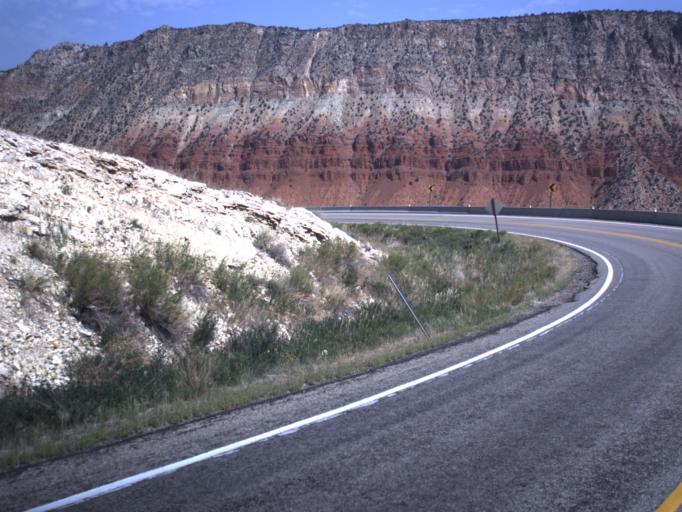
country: US
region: Utah
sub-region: Daggett County
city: Manila
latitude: 40.9145
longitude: -109.6782
